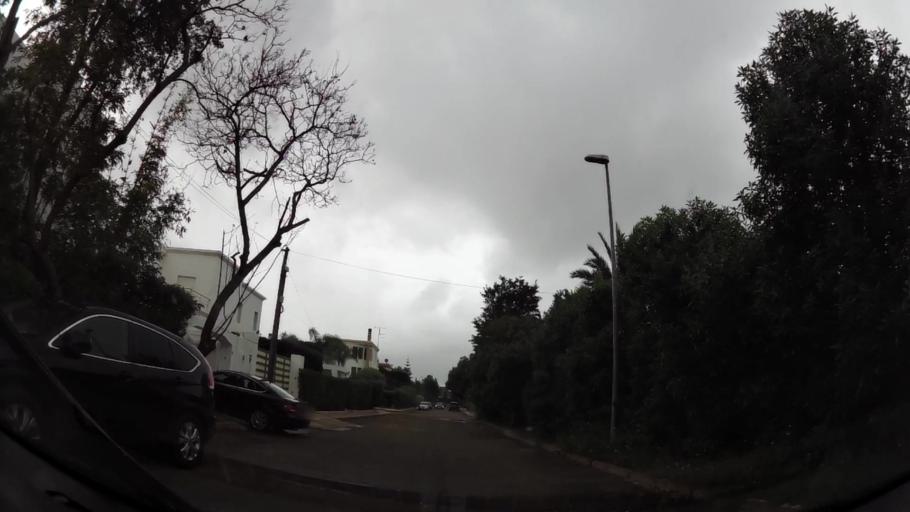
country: MA
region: Grand Casablanca
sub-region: Casablanca
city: Casablanca
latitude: 33.5317
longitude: -7.6199
